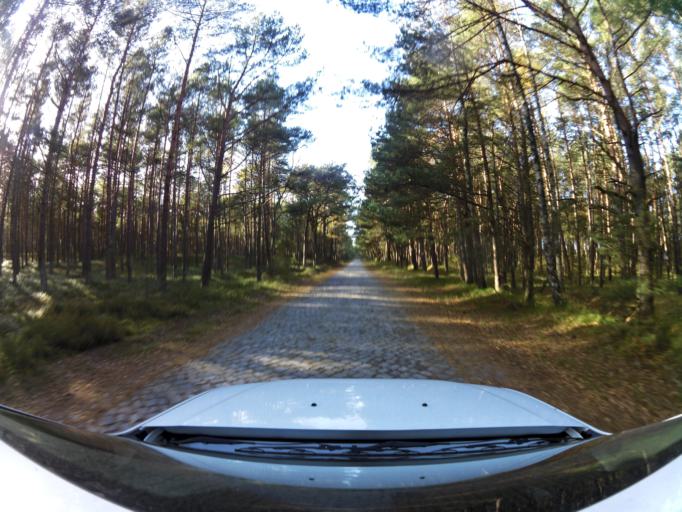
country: PL
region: West Pomeranian Voivodeship
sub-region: Powiat gryficki
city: Trzebiatow
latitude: 54.1227
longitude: 15.1996
